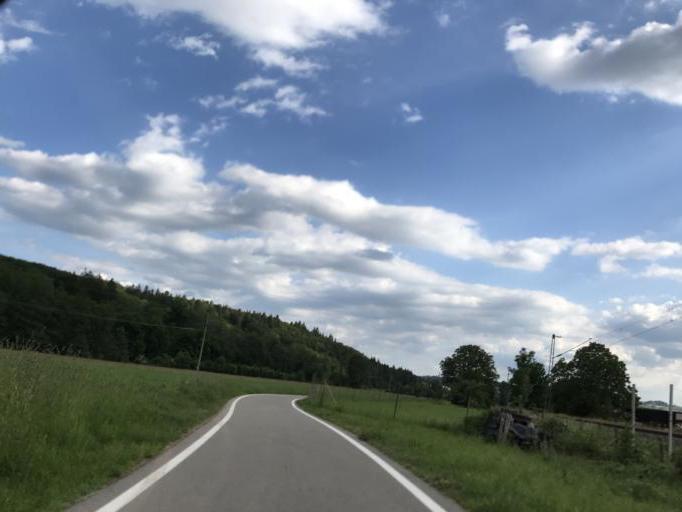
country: DE
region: Baden-Wuerttemberg
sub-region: Freiburg Region
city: Hausen
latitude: 47.6723
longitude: 7.8444
